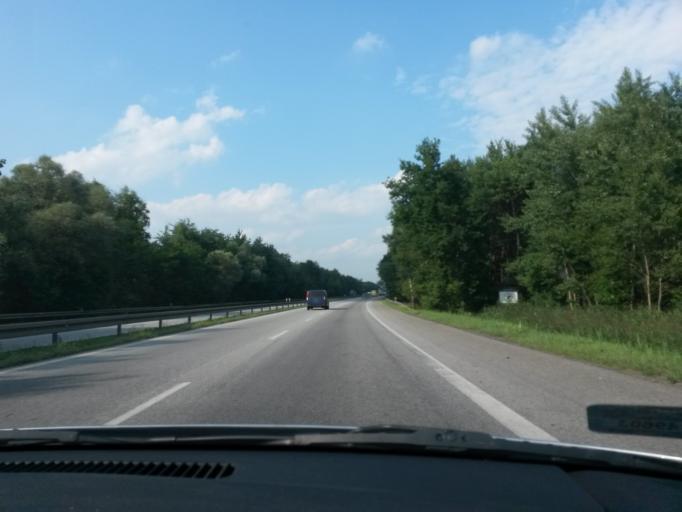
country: PL
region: Silesian Voivodeship
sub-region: Dabrowa Gornicza
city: Dabrowa Gornicza
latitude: 50.2932
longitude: 19.2186
